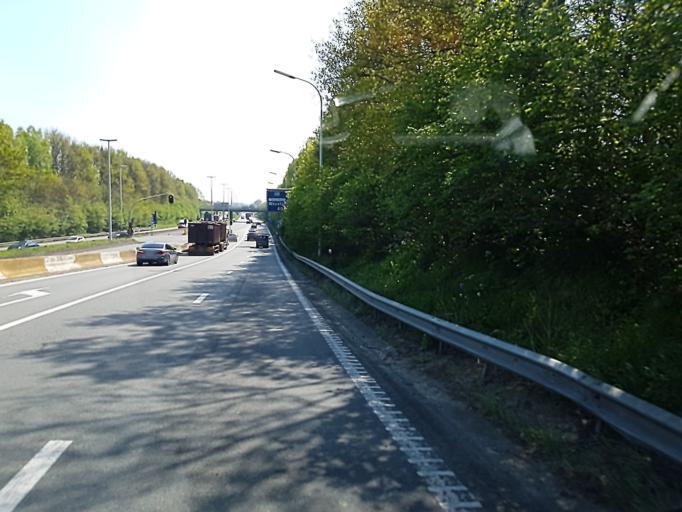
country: BE
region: Flanders
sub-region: Provincie West-Vlaanderen
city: Kortrijk
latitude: 50.8280
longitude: 3.2149
